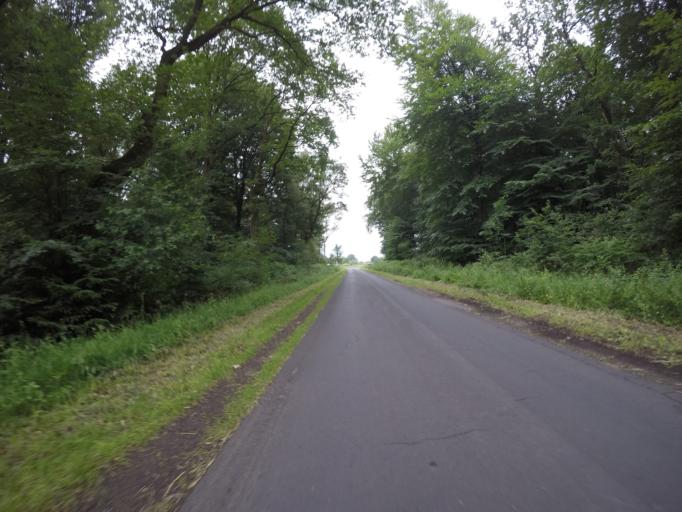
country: DE
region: North Rhine-Westphalia
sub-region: Regierungsbezirk Dusseldorf
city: Hunxe
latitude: 51.6140
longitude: 6.8359
